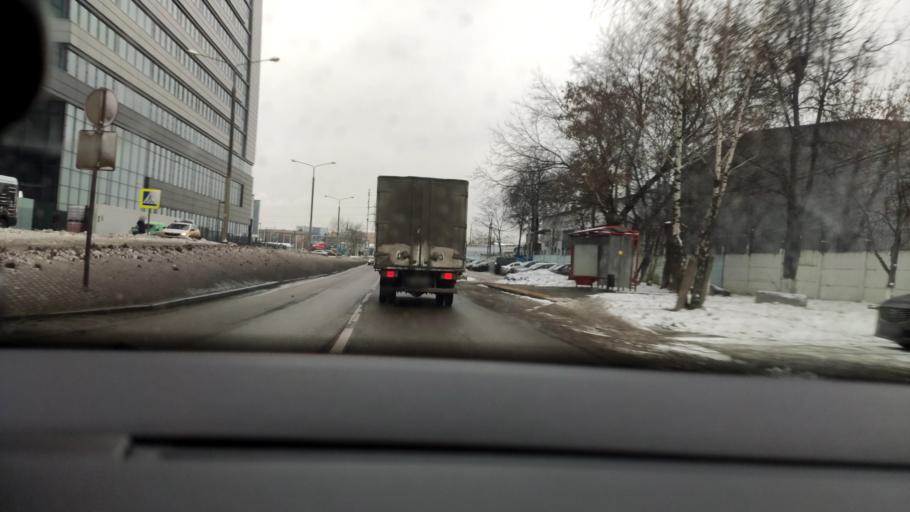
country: RU
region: Moscow
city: Khimki
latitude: 55.9214
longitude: 37.4148
